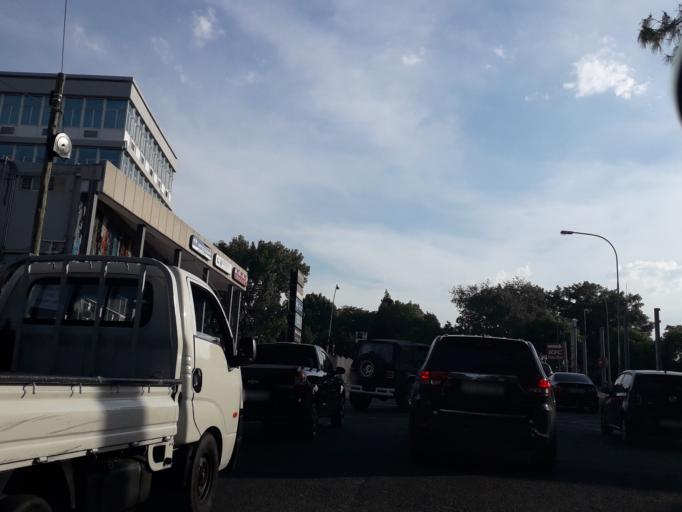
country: ZA
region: Gauteng
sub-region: City of Johannesburg Metropolitan Municipality
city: Johannesburg
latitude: -26.1144
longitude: 28.0222
